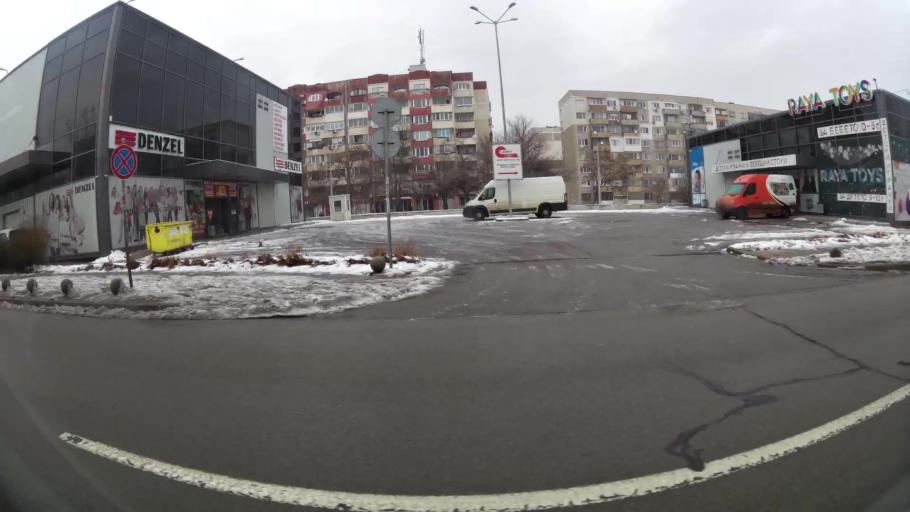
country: BG
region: Sofia-Capital
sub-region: Stolichna Obshtina
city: Sofia
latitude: 42.7114
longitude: 23.3016
